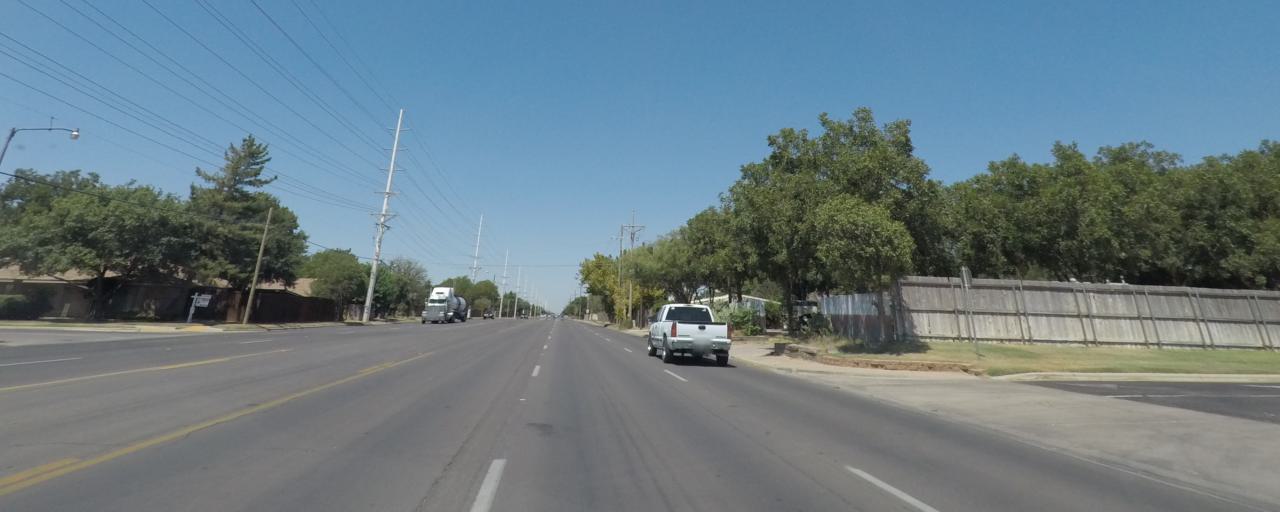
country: US
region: Texas
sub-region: Lubbock County
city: Lubbock
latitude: 33.5081
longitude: -101.8875
